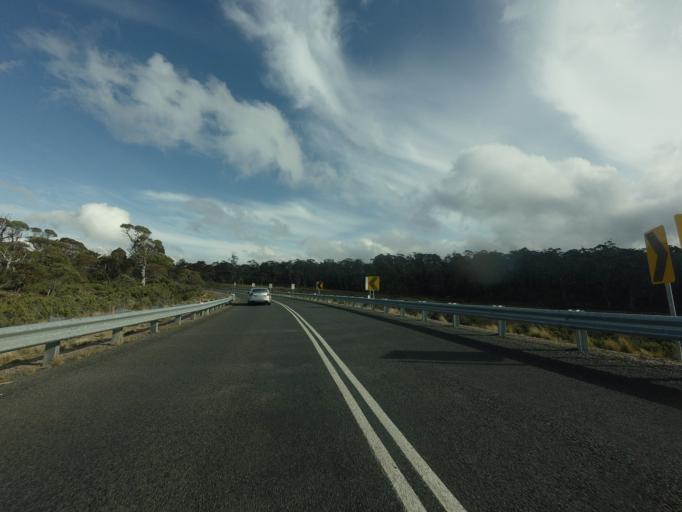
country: AU
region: Tasmania
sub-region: Meander Valley
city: Deloraine
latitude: -41.7867
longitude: 146.6930
